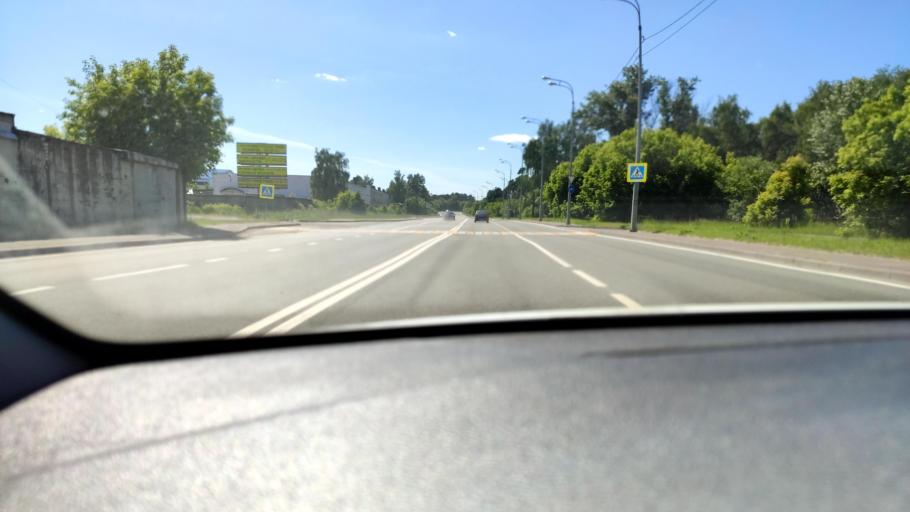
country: RU
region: Tatarstan
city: Staroye Arakchino
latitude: 55.8368
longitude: 49.0318
